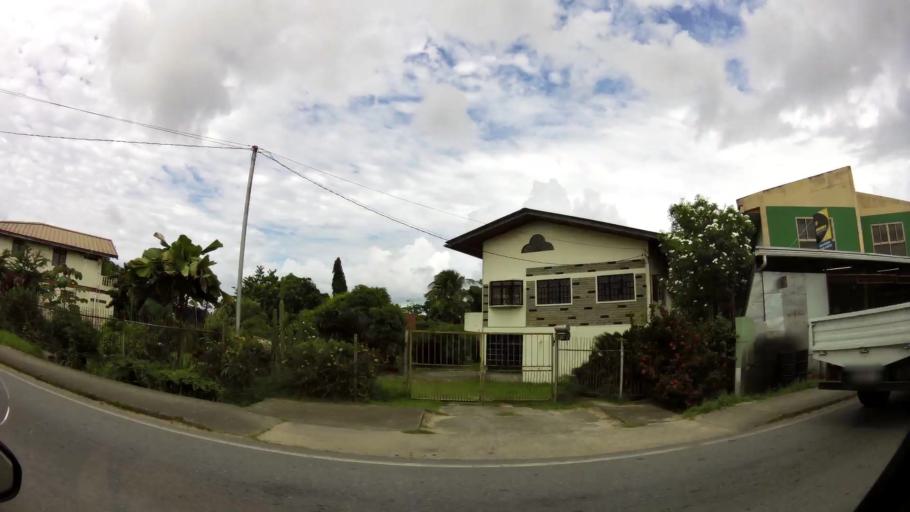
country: TT
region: Couva-Tabaquite-Talparo
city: Couva
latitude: 10.4467
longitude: -61.4460
